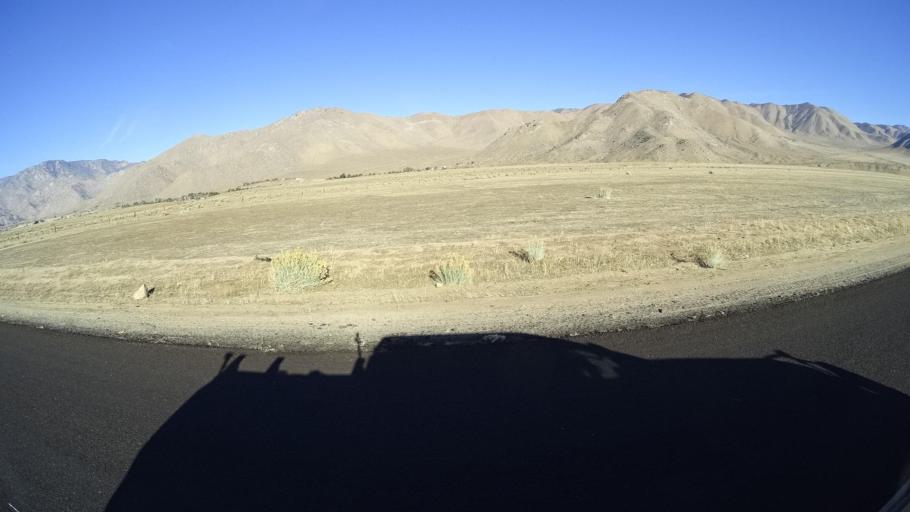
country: US
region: California
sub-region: Kern County
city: Weldon
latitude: 35.6227
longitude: -118.2595
